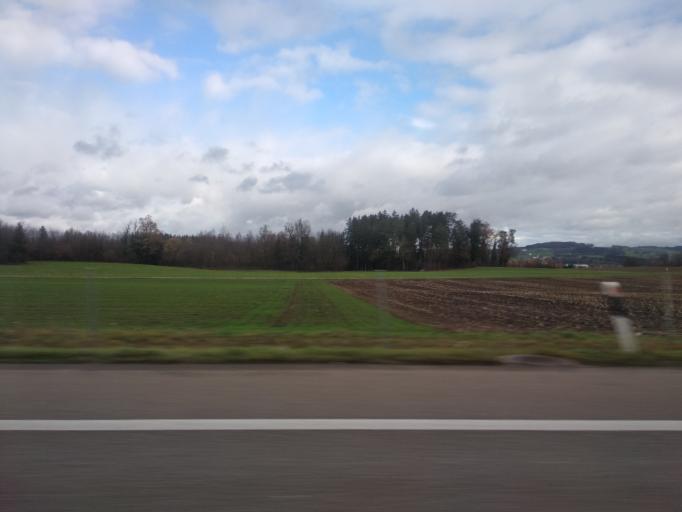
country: CH
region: Thurgau
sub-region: Muenchwilen District
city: Munchwilen
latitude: 47.4784
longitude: 8.9775
